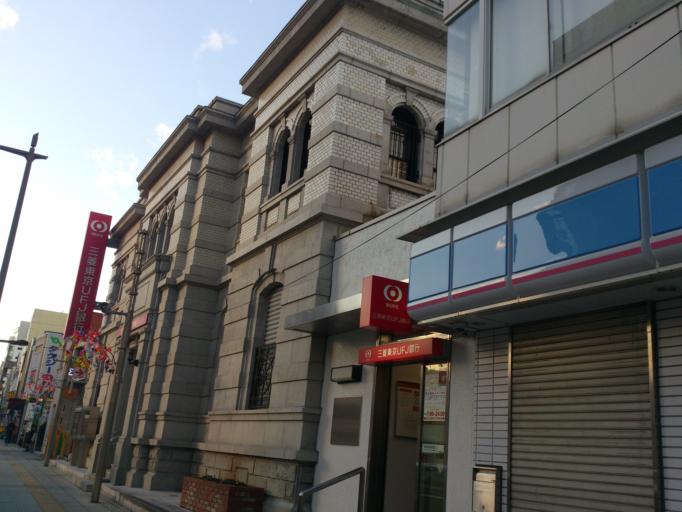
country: JP
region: Ibaraki
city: Mito-shi
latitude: 36.3794
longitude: 140.4620
